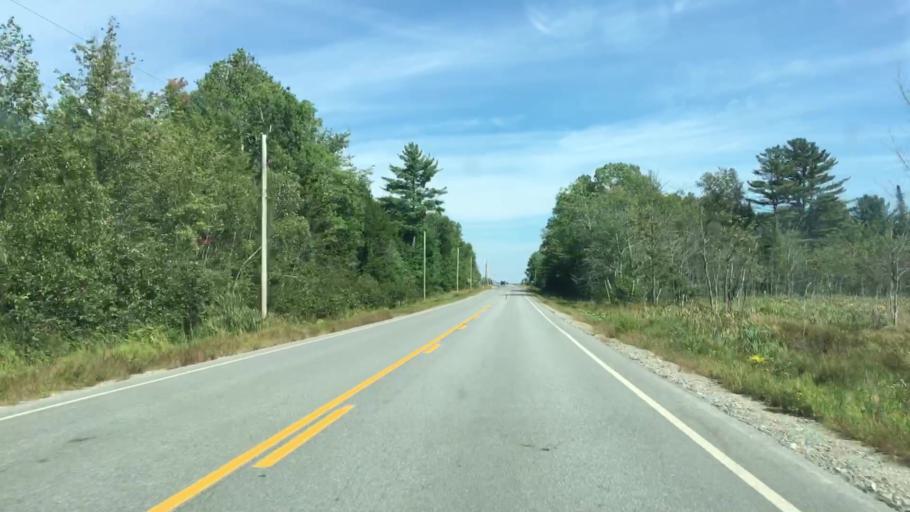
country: US
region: Maine
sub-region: Penobscot County
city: Howland
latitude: 45.2342
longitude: -68.6864
